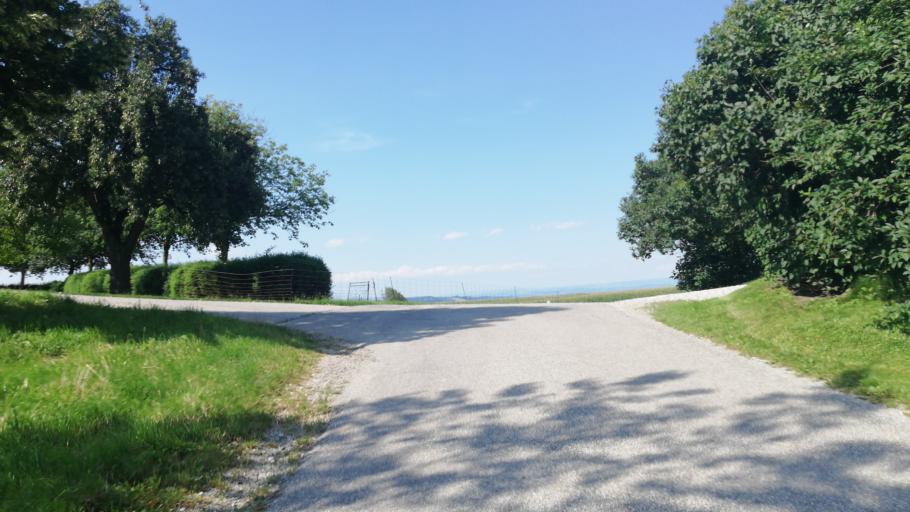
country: AT
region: Upper Austria
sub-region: Wels-Land
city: Gunskirchen
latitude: 48.1733
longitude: 13.9218
